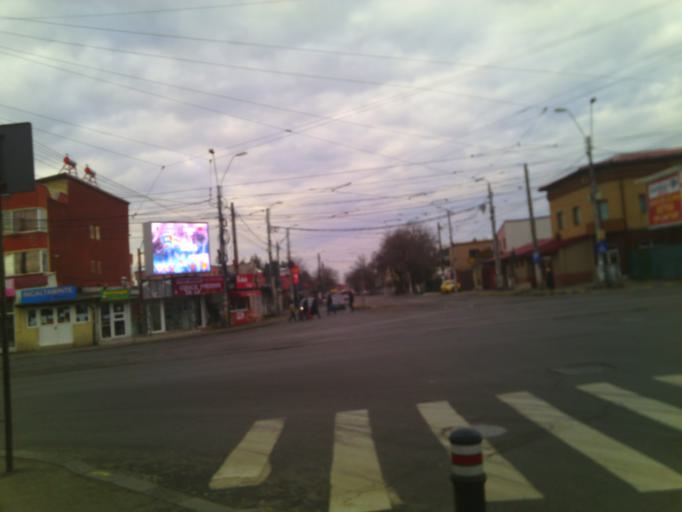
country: RO
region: Ilfov
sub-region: Comuna Jilava
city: Jilava
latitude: 44.3788
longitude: 26.0921
